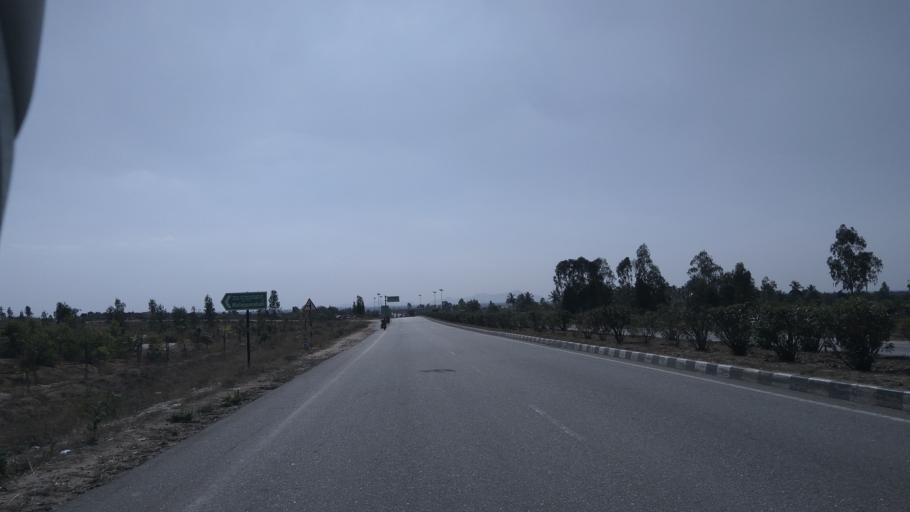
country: IN
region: Karnataka
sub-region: Kolar
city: Mulbagal
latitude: 13.1497
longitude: 78.2979
